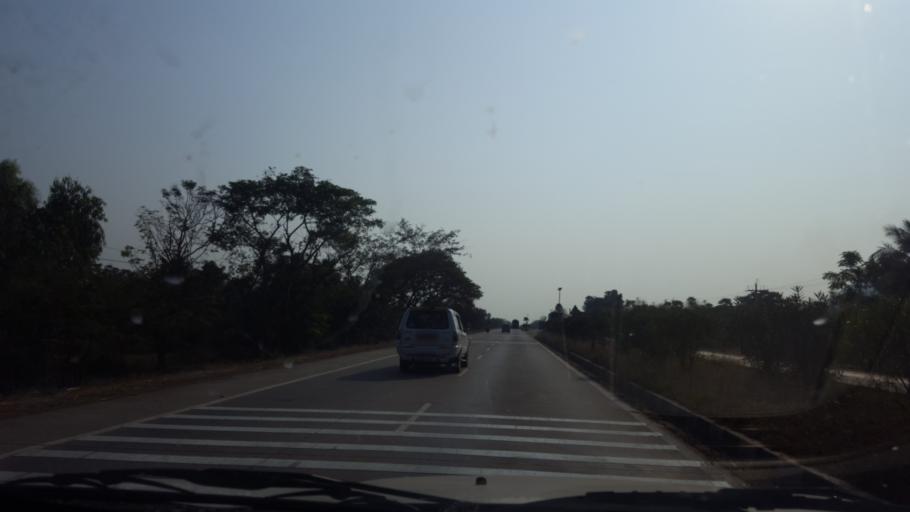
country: IN
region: Andhra Pradesh
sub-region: Vishakhapatnam
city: Elamanchili
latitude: 17.5520
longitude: 82.8424
